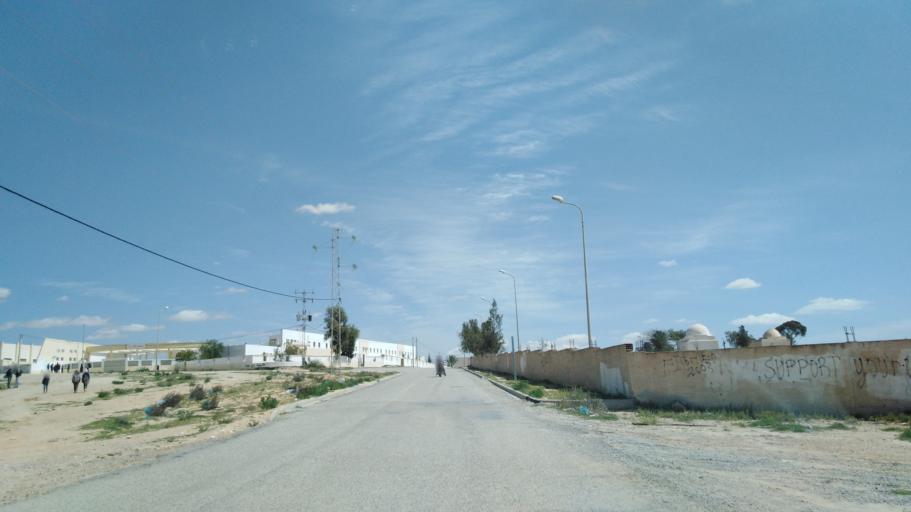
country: TN
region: Safaqis
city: Sfax
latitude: 34.7401
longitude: 10.5394
